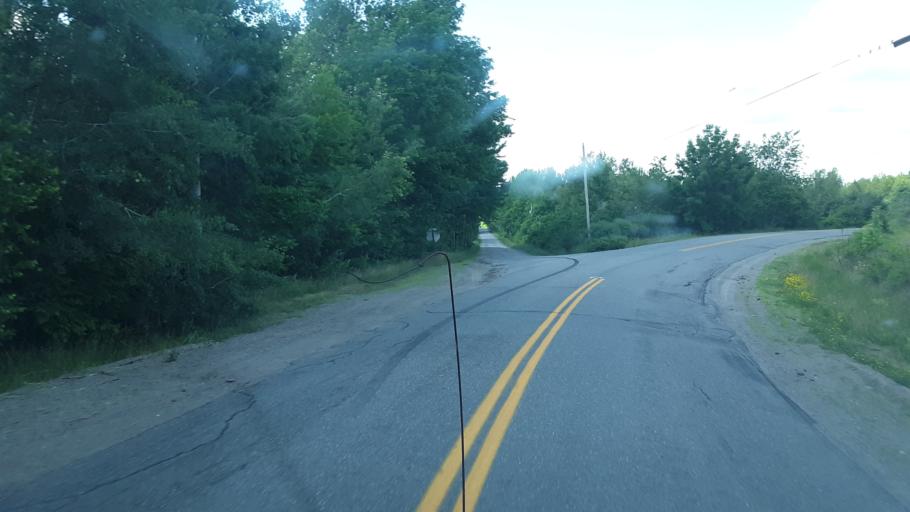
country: US
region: Maine
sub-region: Washington County
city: Calais
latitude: 45.1010
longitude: -67.5112
